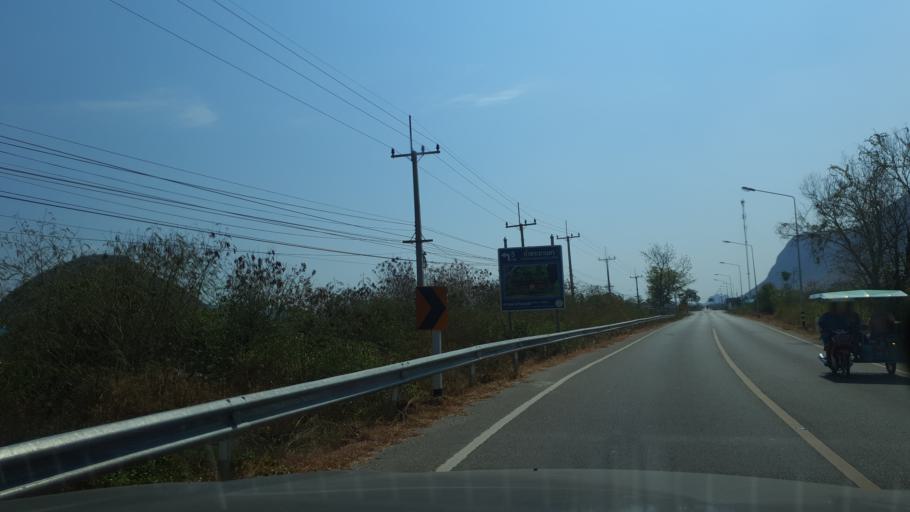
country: TH
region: Prachuap Khiri Khan
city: Sam Roi Yot
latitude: 12.1996
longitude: 99.9804
